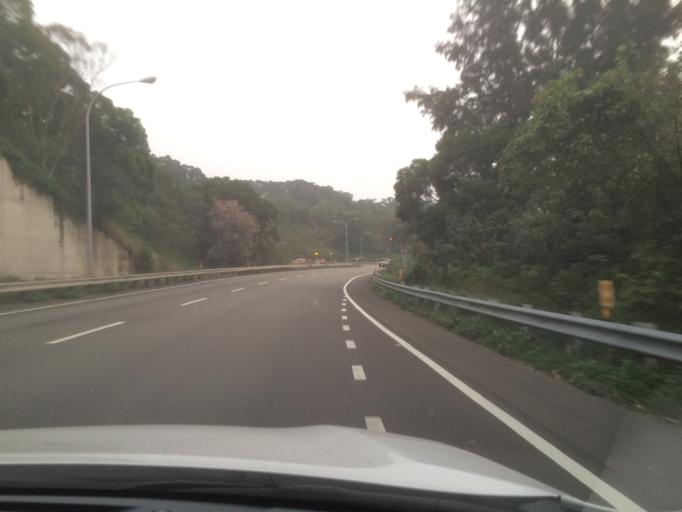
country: TW
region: Taiwan
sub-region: Hsinchu
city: Hsinchu
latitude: 24.7544
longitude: 120.9844
